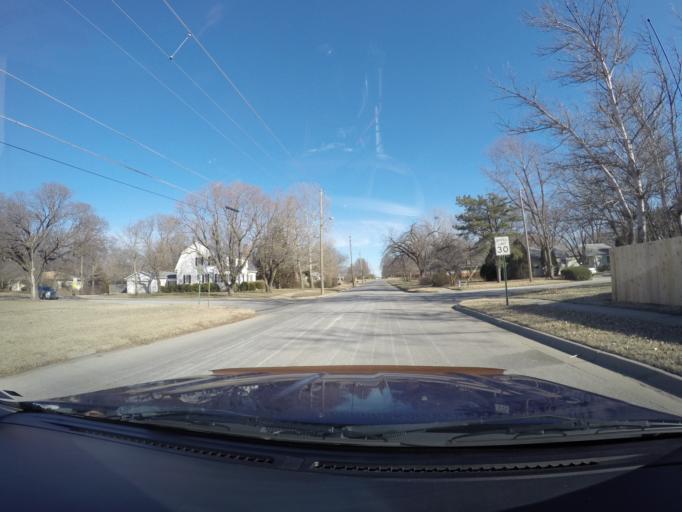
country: US
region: Kansas
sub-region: Harvey County
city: North Newton
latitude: 38.0718
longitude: -97.3446
